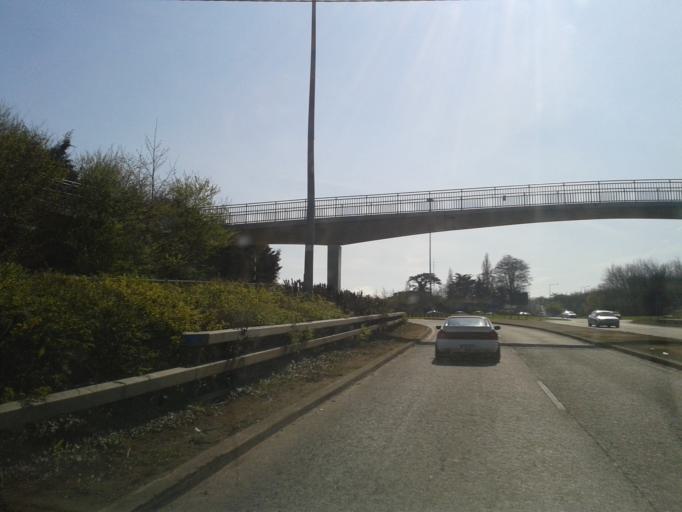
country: IE
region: Leinster
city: Loughlinstown
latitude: 53.2424
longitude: -6.1301
